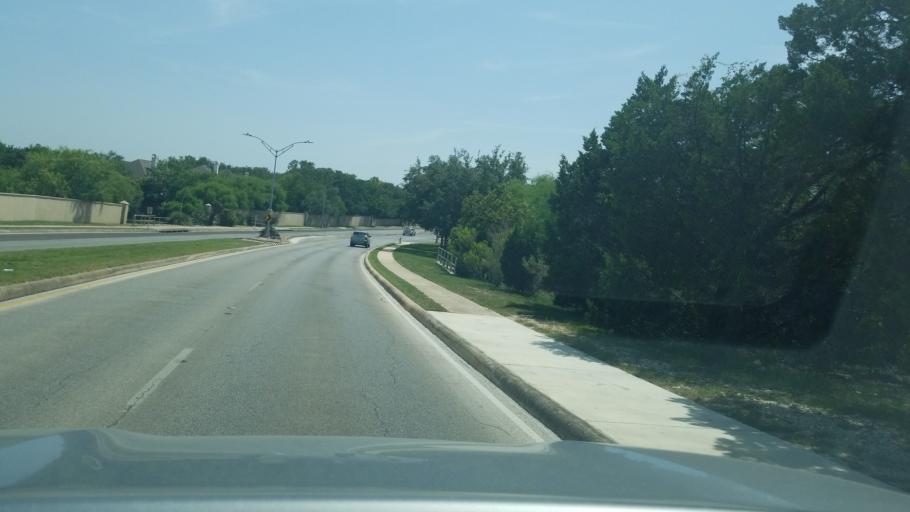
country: US
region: Texas
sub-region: Bexar County
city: Hollywood Park
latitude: 29.6167
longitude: -98.5172
